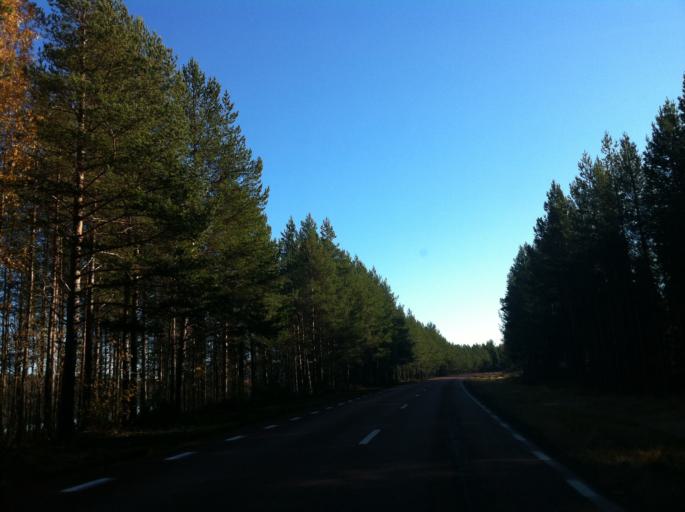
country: SE
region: Dalarna
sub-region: Alvdalens Kommun
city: AElvdalen
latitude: 61.3055
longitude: 13.7237
